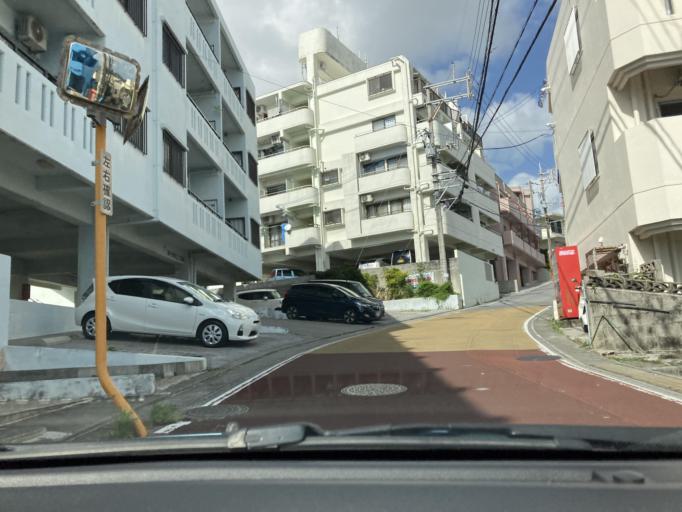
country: JP
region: Okinawa
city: Naha-shi
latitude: 26.2002
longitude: 127.7049
